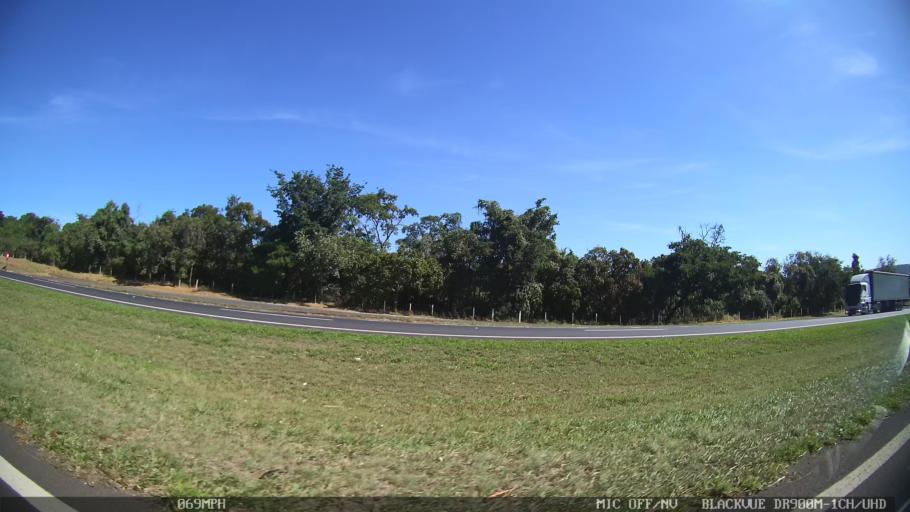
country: BR
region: Sao Paulo
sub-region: Sao Simao
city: Sao Simao
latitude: -21.5469
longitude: -47.6392
